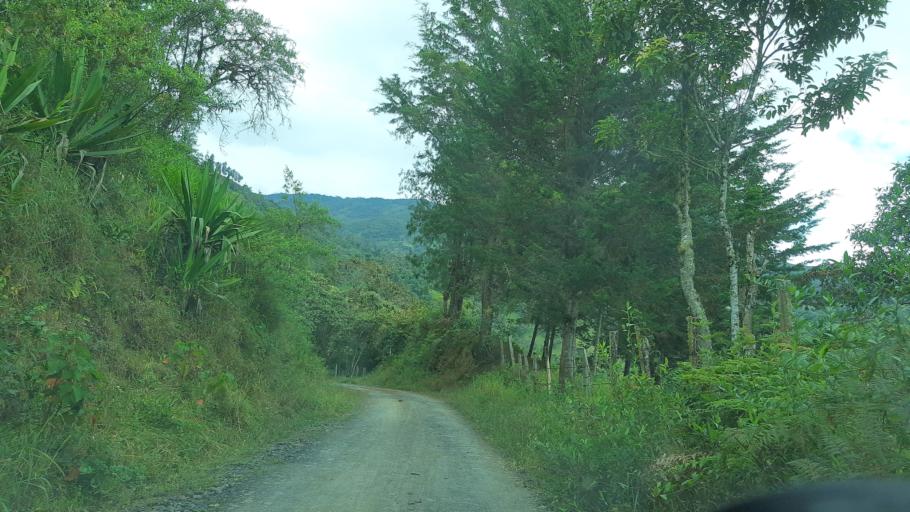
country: CO
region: Boyaca
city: Garagoa
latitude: 5.0307
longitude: -73.3318
